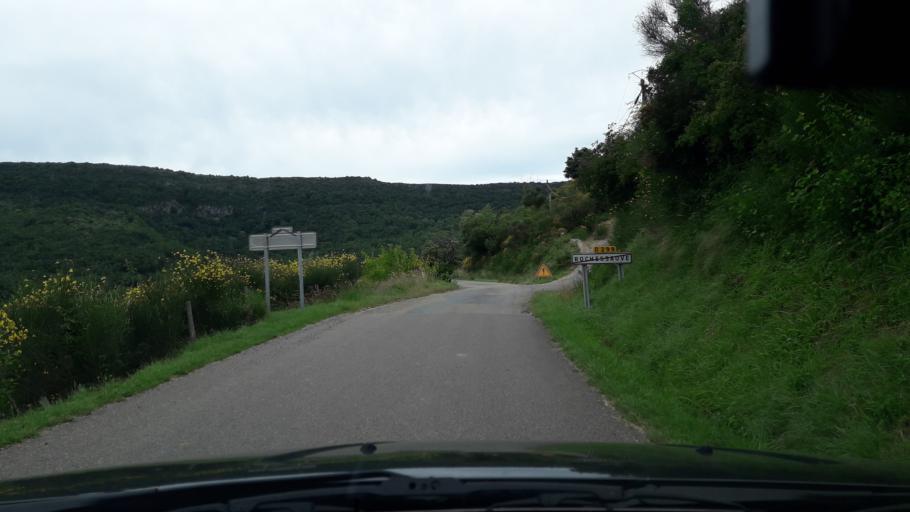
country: FR
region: Rhone-Alpes
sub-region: Departement de l'Ardeche
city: Alissas
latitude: 44.6775
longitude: 4.6250
